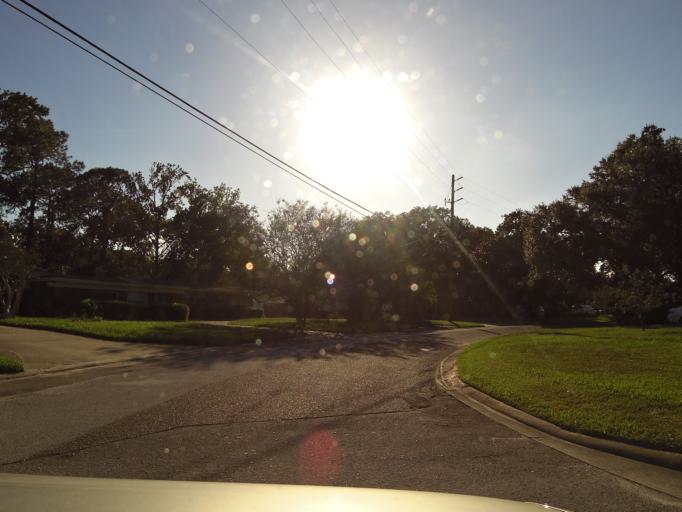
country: US
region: Florida
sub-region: Duval County
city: Jacksonville
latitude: 30.2478
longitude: -81.6269
